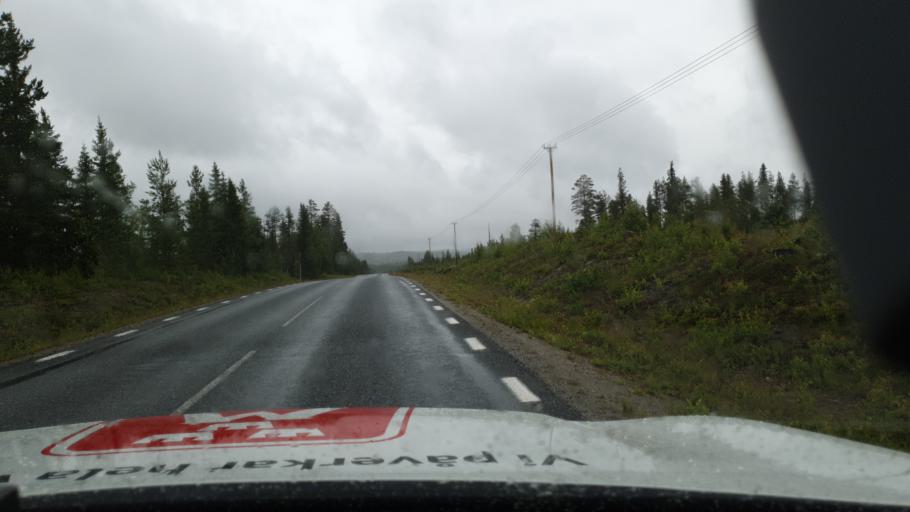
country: SE
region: Vaesterbotten
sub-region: Asele Kommun
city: Insjon
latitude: 64.3065
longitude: 17.6908
